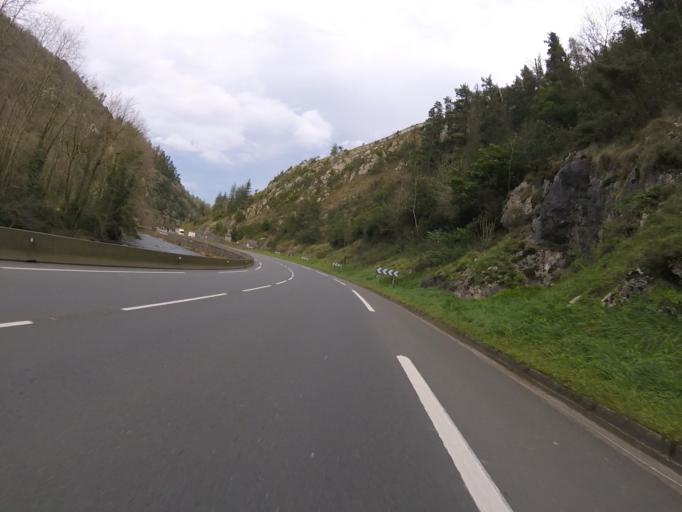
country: ES
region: Basque Country
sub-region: Provincia de Guipuzcoa
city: Cestona
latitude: 43.2440
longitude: -2.2584
